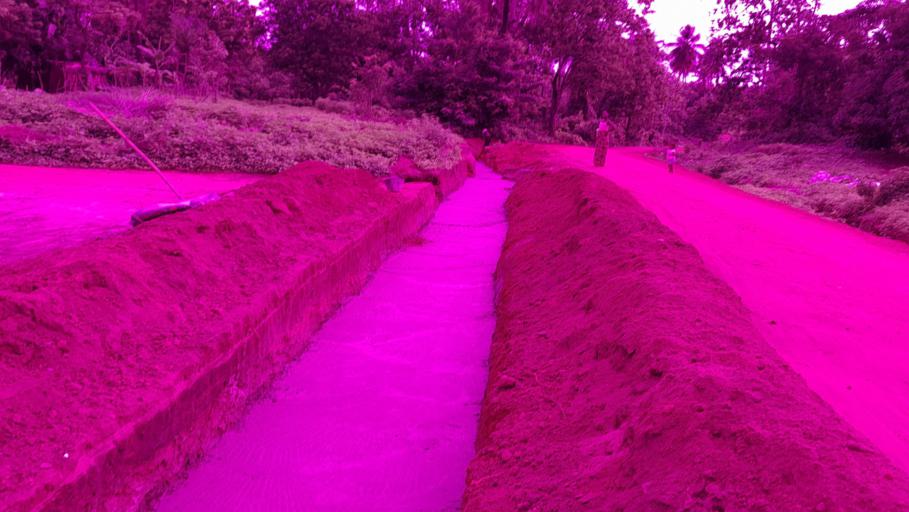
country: GN
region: Boke
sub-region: Boffa
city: Boffa
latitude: 10.0258
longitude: -13.8846
